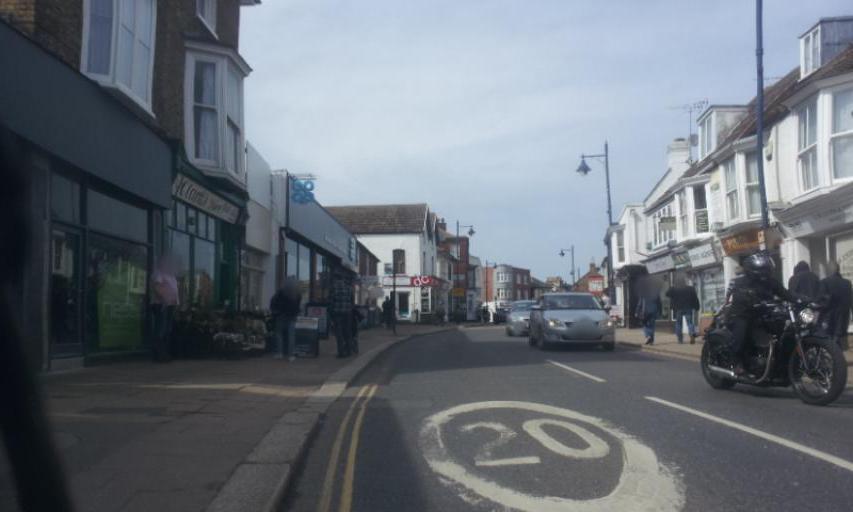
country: GB
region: England
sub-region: Kent
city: Whitstable
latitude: 51.3551
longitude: 1.0249
